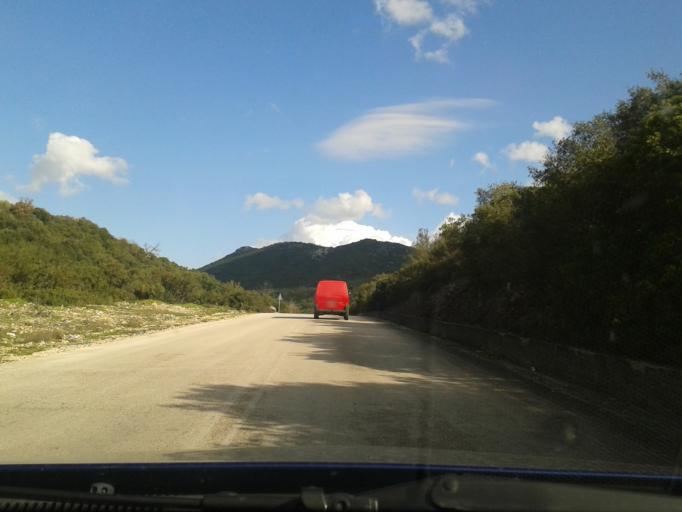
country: GR
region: West Greece
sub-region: Nomos Aitolias kai Akarnanias
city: Astakos
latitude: 38.5983
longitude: 21.1036
